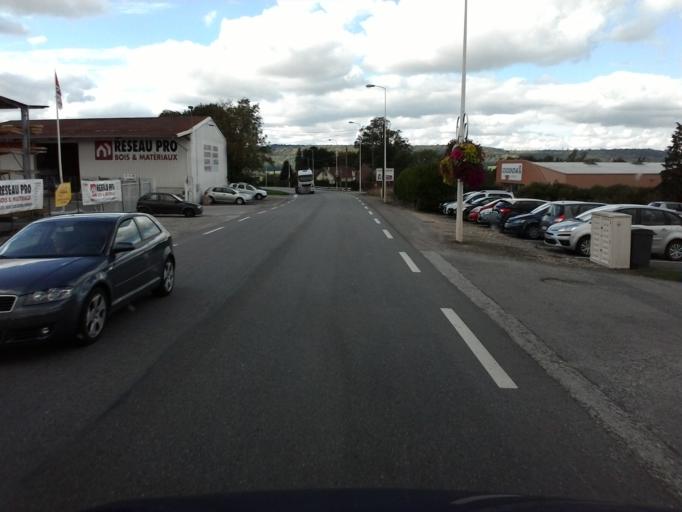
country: FR
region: Lorraine
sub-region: Departement des Vosges
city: Neufchateau
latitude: 48.3682
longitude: 5.7000
